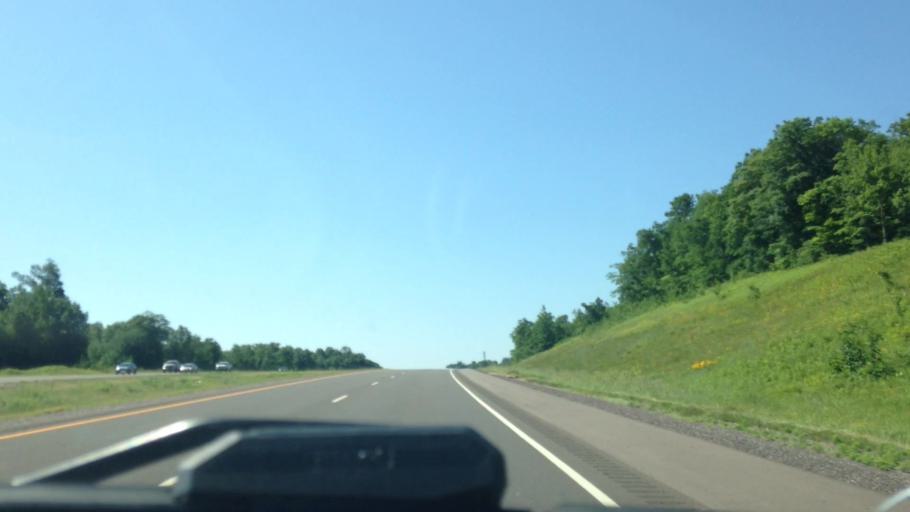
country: US
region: Wisconsin
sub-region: Washburn County
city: Spooner
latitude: 45.9727
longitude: -91.8275
